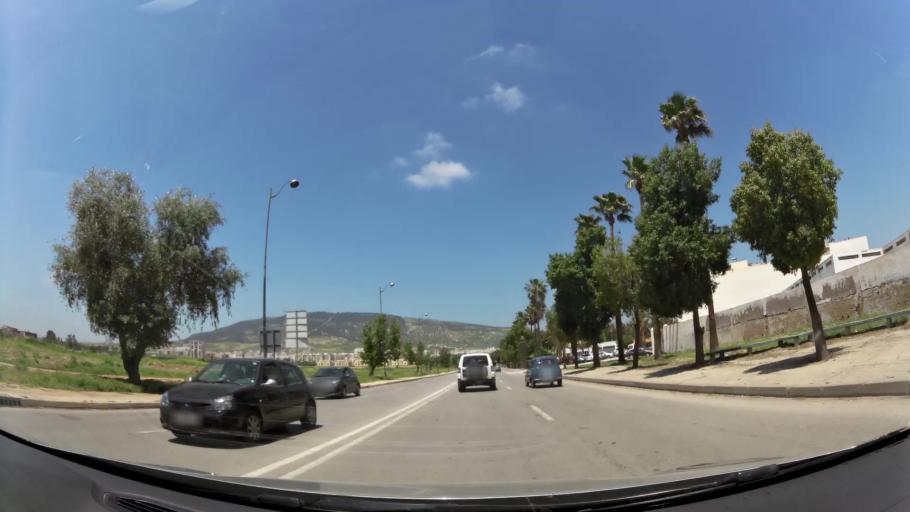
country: MA
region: Fes-Boulemane
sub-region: Fes
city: Fes
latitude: 34.0425
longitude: -5.0355
